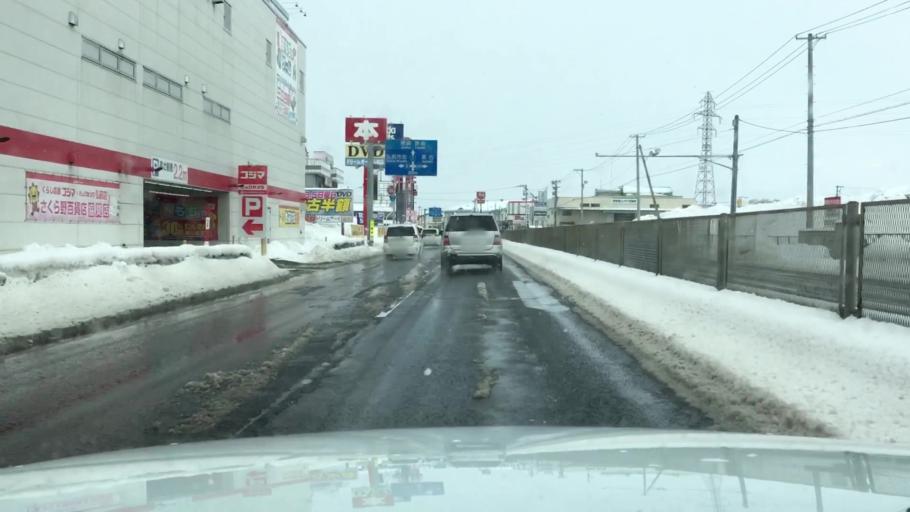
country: JP
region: Aomori
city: Hirosaki
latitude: 40.6076
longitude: 140.4989
